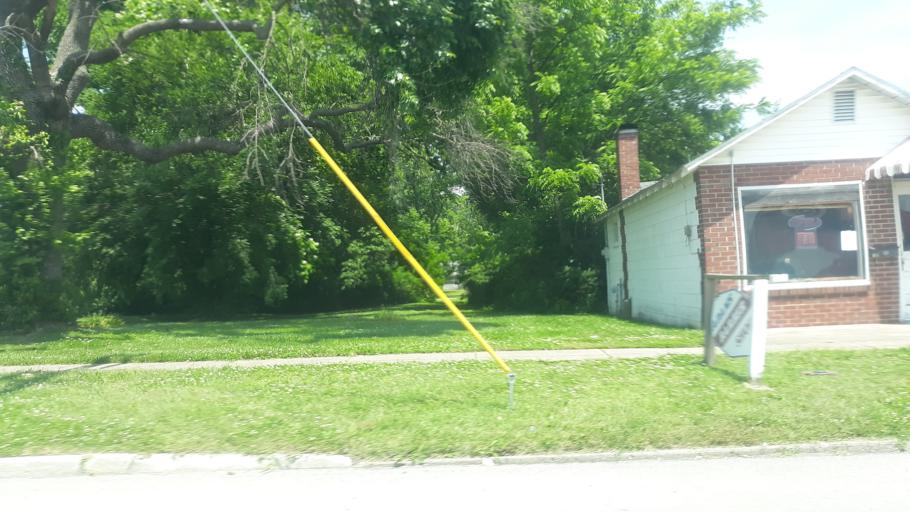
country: US
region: Illinois
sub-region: Saline County
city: Harrisburg
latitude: 37.7391
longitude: -88.5340
